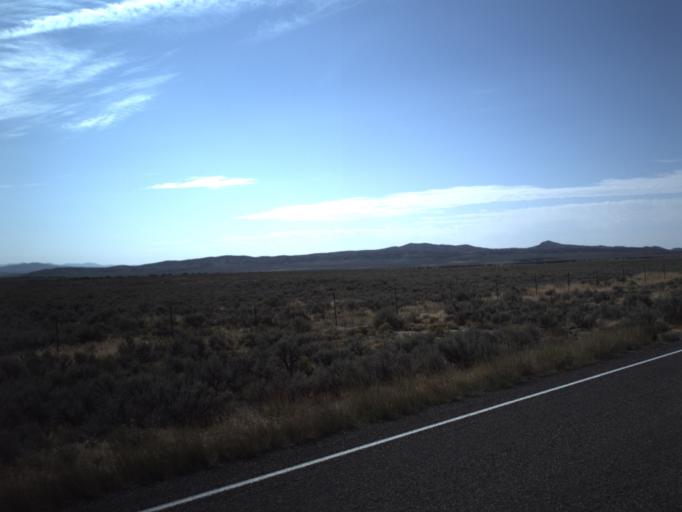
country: US
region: Idaho
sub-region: Cassia County
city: Burley
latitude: 41.7448
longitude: -113.5180
